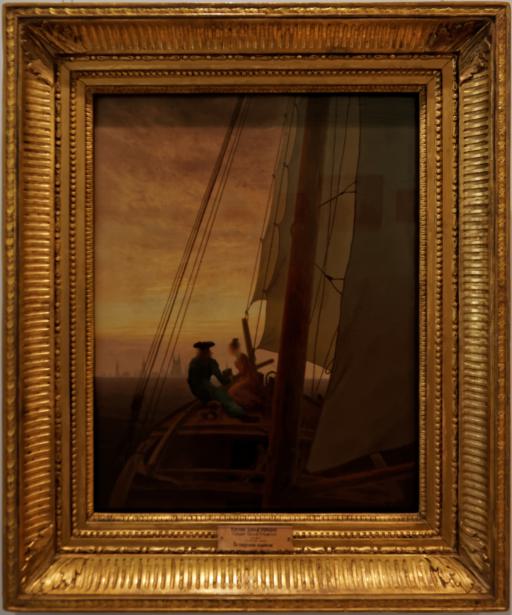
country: RU
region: St.-Petersburg
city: Saint Petersburg
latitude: 59.9385
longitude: 30.3188
